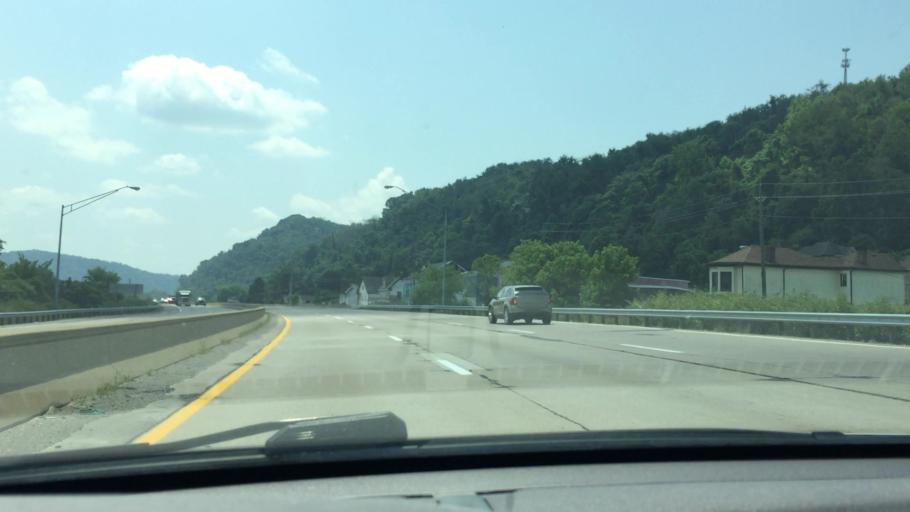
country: US
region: Ohio
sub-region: Belmont County
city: Bellaire
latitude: 40.0065
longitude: -80.7445
